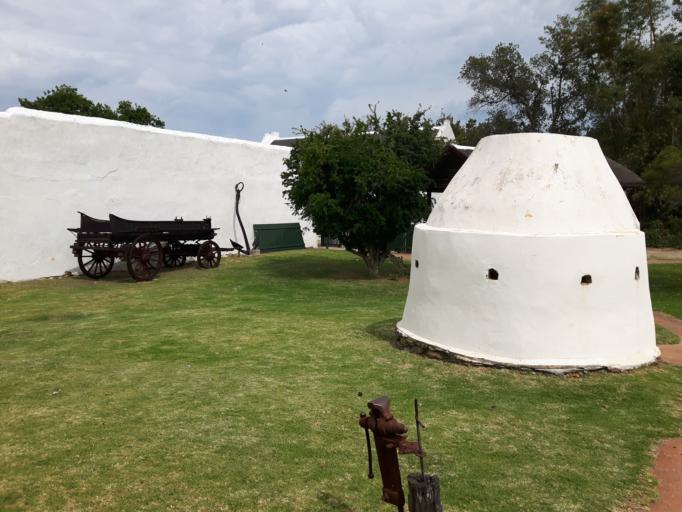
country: ZA
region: Western Cape
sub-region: Overberg District Municipality
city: Swellendam
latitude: -34.0184
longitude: 20.4532
